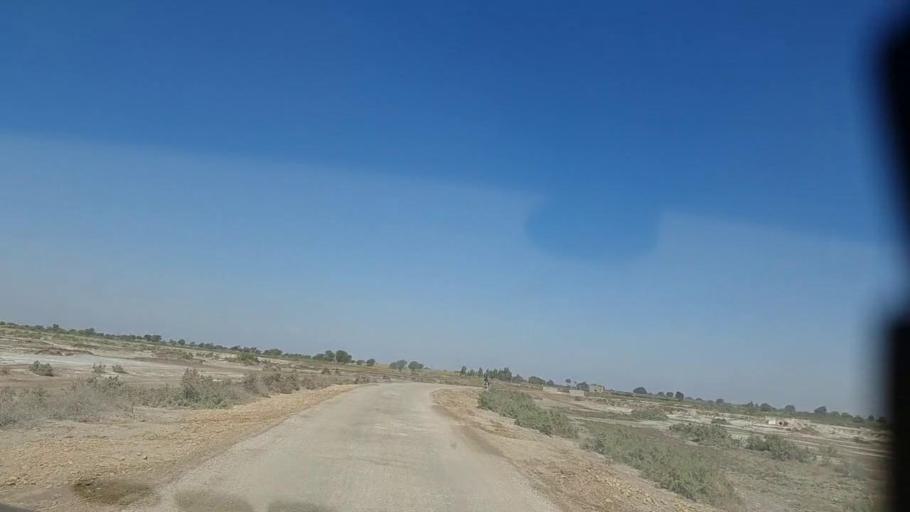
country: PK
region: Sindh
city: Digri
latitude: 25.1651
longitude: 69.0487
